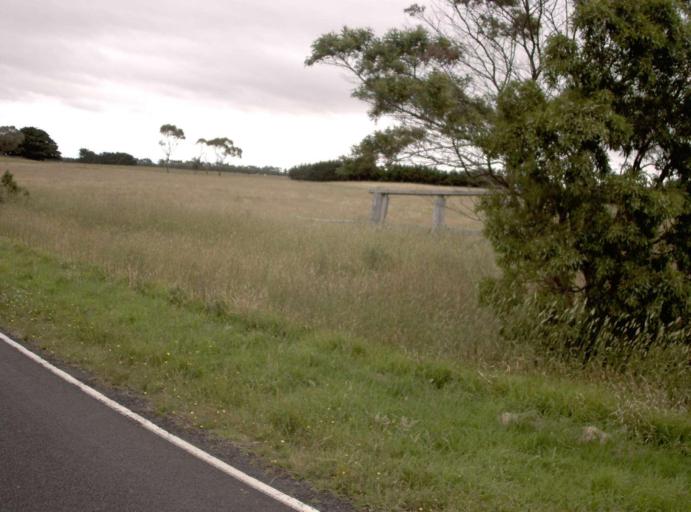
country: AU
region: Victoria
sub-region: Wellington
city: Sale
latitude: -38.5375
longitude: 146.8886
